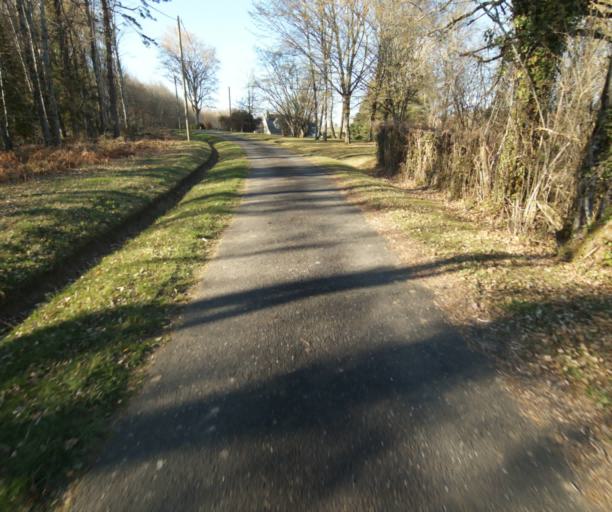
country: FR
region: Limousin
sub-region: Departement de la Correze
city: Seilhac
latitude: 45.3870
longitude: 1.6982
